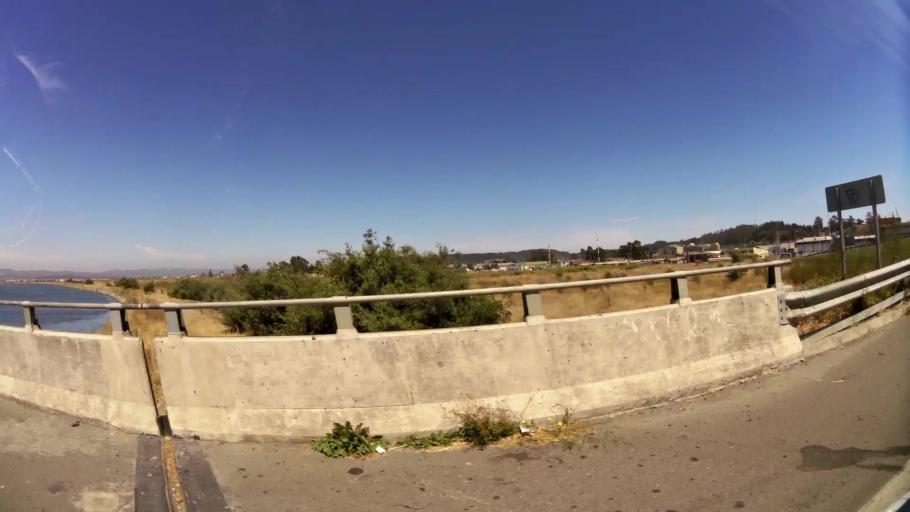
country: CL
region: Biobio
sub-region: Provincia de Concepcion
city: Talcahuano
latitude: -36.7321
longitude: -73.1049
